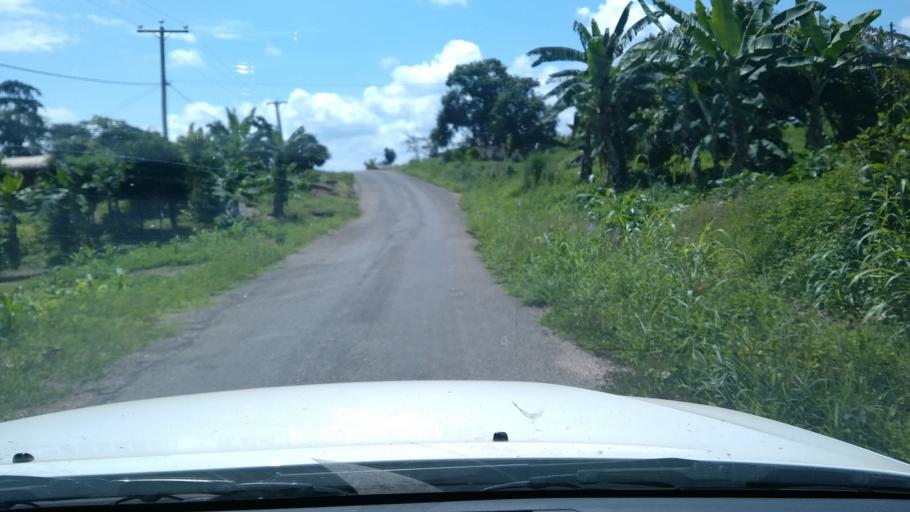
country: CM
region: Centre
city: Evodoula
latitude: 4.1455
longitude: 11.2755
